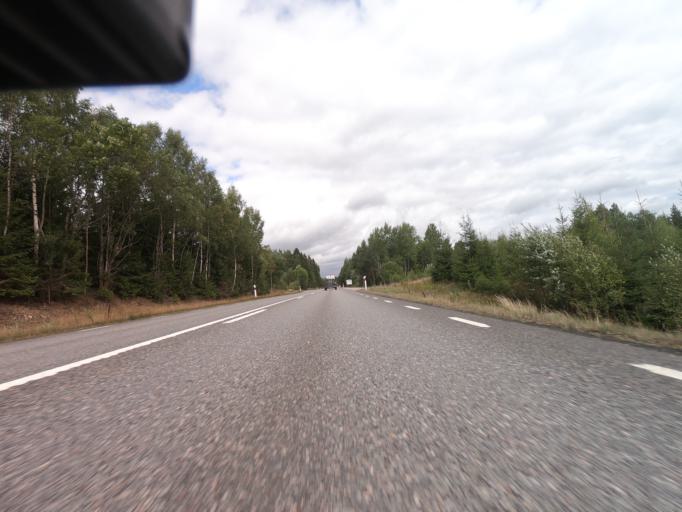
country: SE
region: Joenkoeping
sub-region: Vaggeryds Kommun
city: Vaggeryd
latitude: 57.5068
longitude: 14.2815
